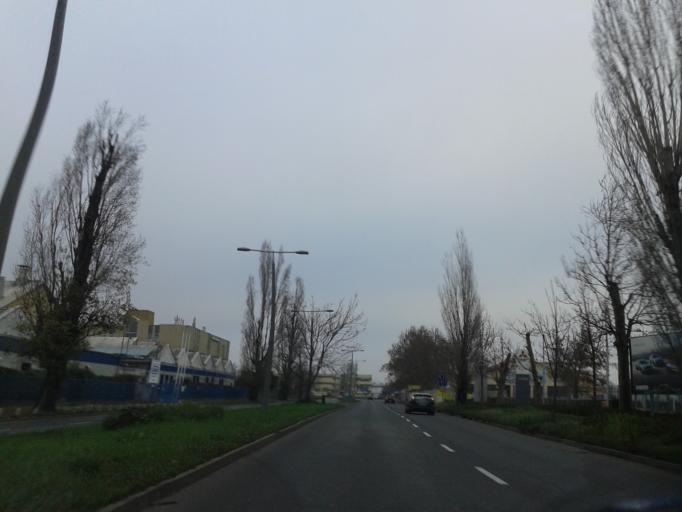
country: HU
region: Budapest
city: Budapest XXII. keruelet
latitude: 47.4451
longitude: 19.0457
